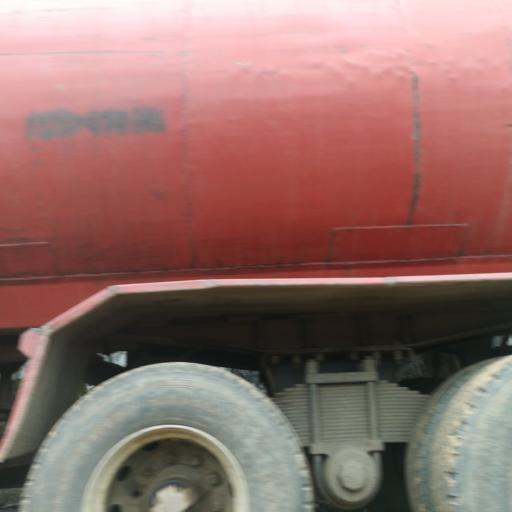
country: NG
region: Rivers
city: Port Harcourt
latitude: 4.8181
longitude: 7.0434
